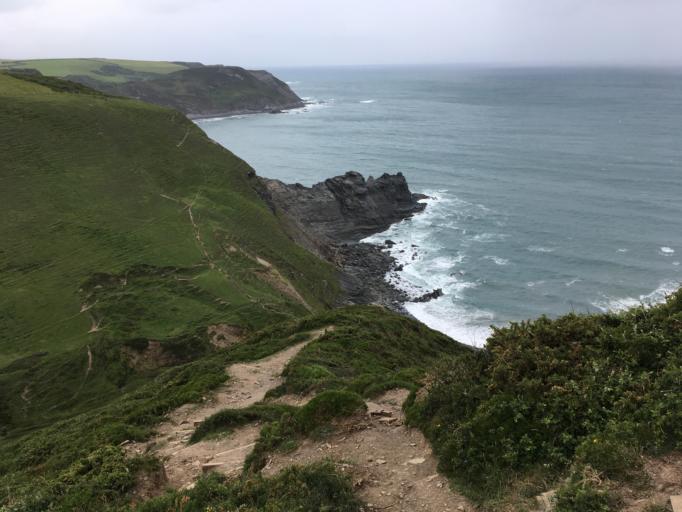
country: GB
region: England
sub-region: Cornwall
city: Poundstock
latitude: 50.7581
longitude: -4.6127
